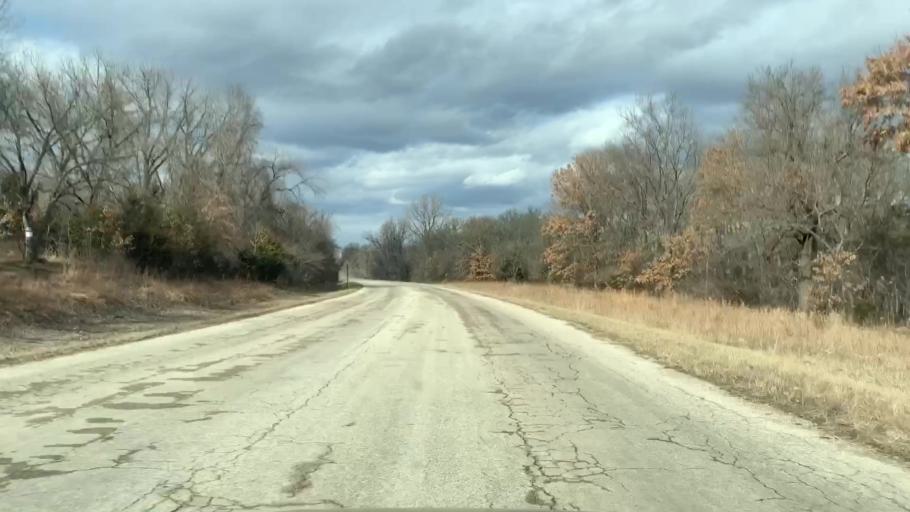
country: US
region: Kansas
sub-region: Allen County
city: Humboldt
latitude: 37.7493
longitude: -95.4703
